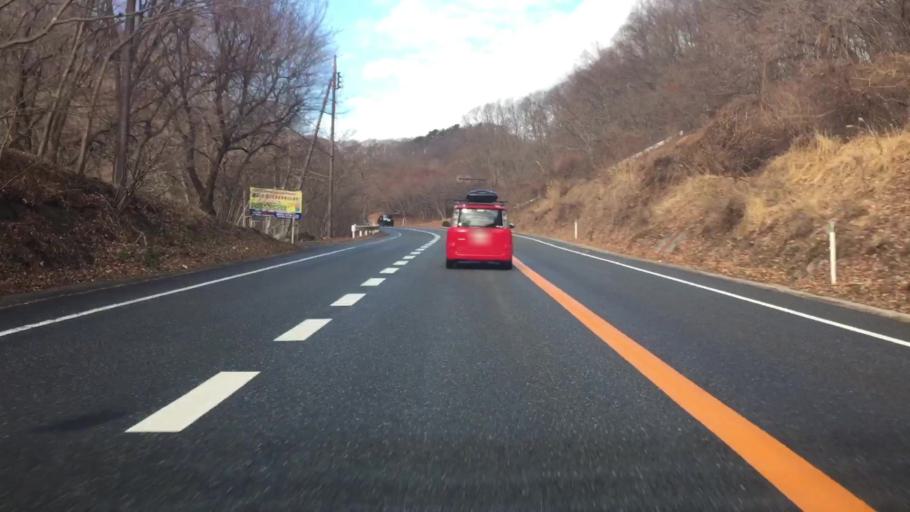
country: JP
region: Nagano
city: Saku
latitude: 36.3023
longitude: 138.6716
